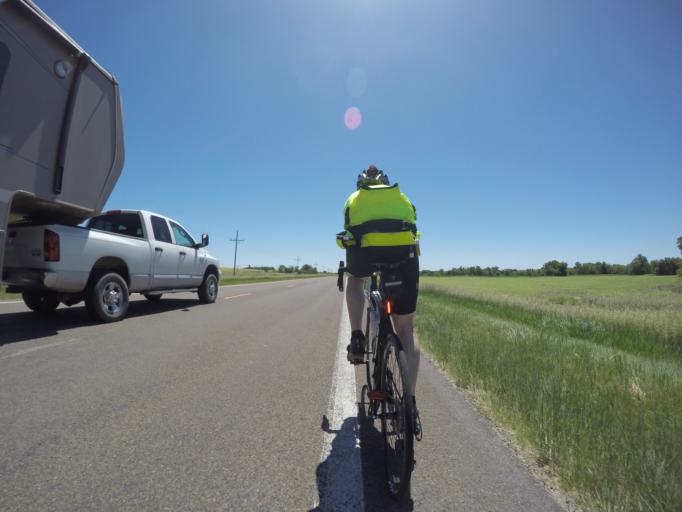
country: US
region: Kansas
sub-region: Phillips County
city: Phillipsburg
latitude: 39.8162
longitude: -99.5245
